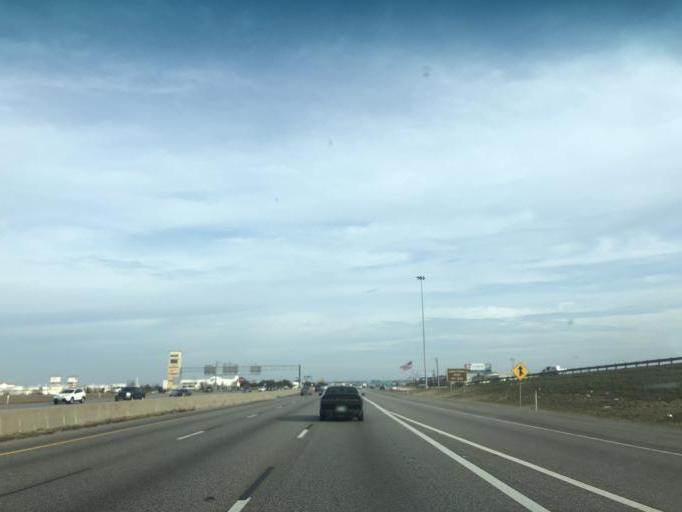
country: US
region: Texas
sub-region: Tarrant County
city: Arlington
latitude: 32.6772
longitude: -97.0584
